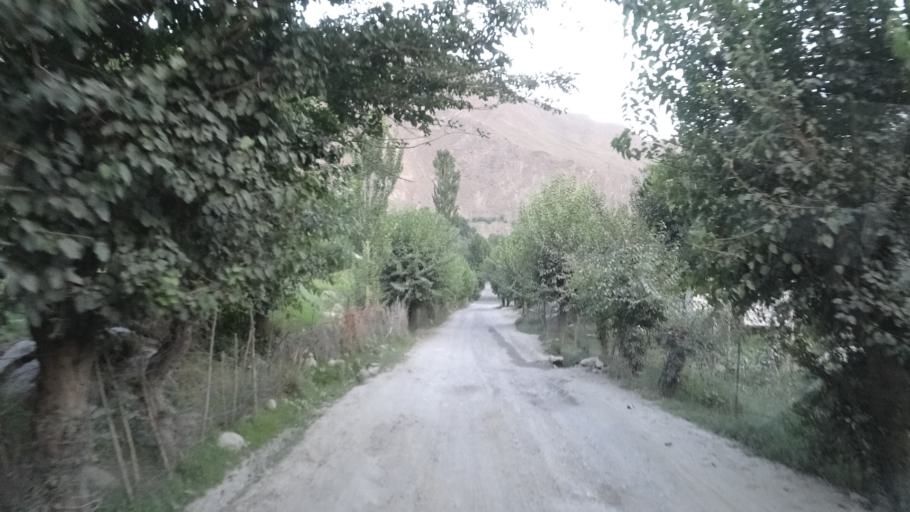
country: AF
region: Badakhshan
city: Maymay
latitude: 38.4235
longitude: 71.1047
